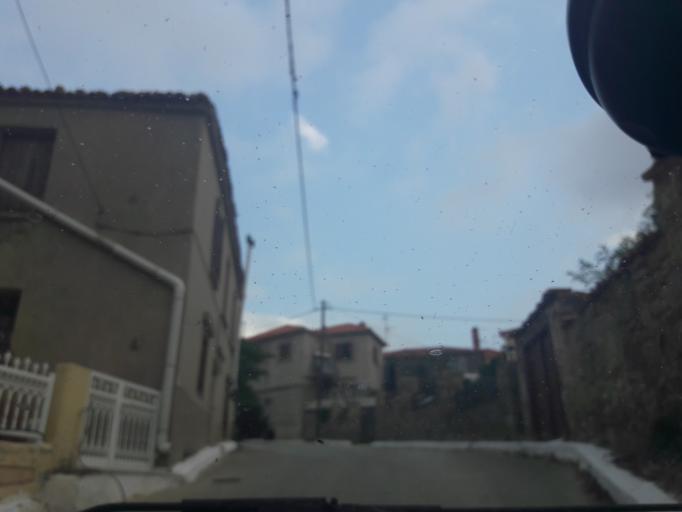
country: GR
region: North Aegean
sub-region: Nomos Lesvou
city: Myrina
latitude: 39.9496
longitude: 25.1656
